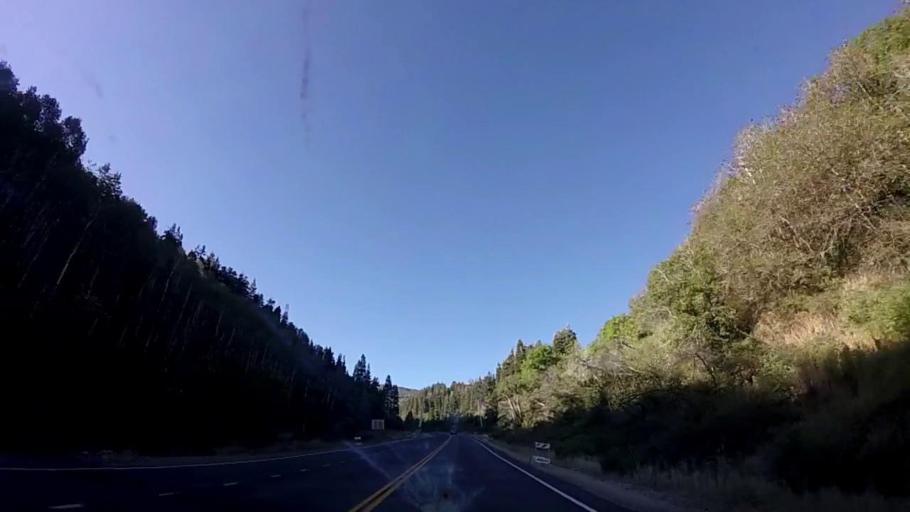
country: US
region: Utah
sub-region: Summit County
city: Park City
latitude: 40.6366
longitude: -111.4938
